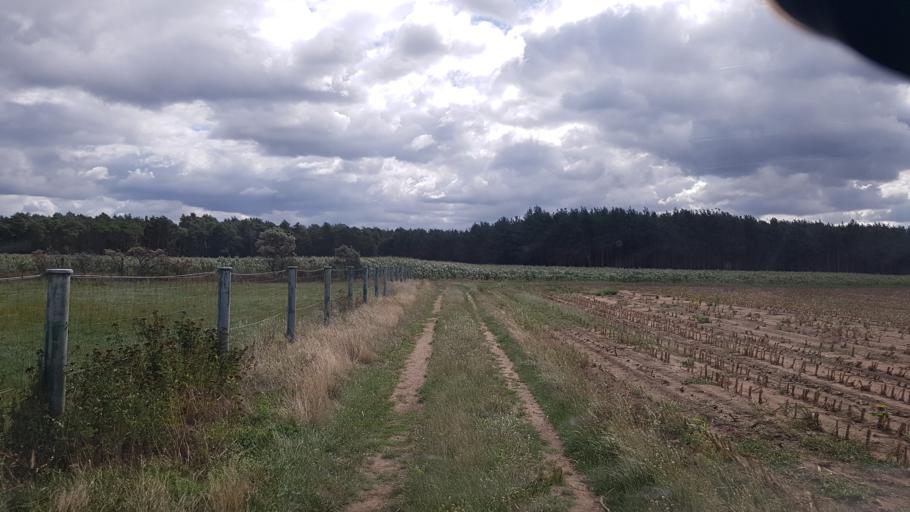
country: DE
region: Brandenburg
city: Bad Liebenwerda
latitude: 51.5457
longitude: 13.3357
